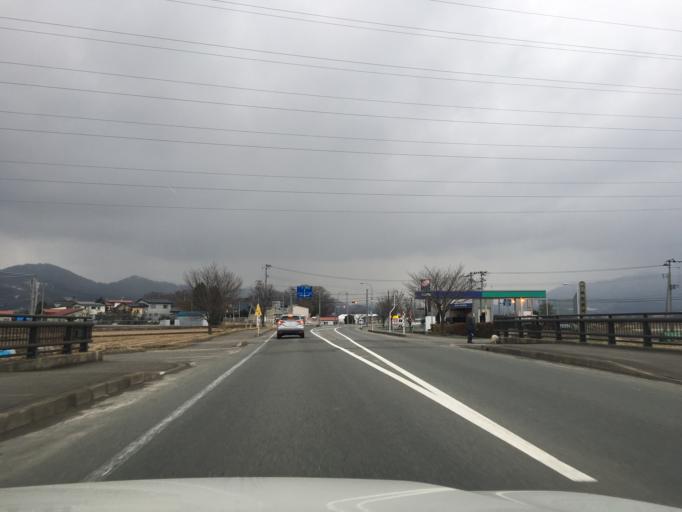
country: JP
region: Aomori
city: Kuroishi
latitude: 40.5741
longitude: 140.5683
